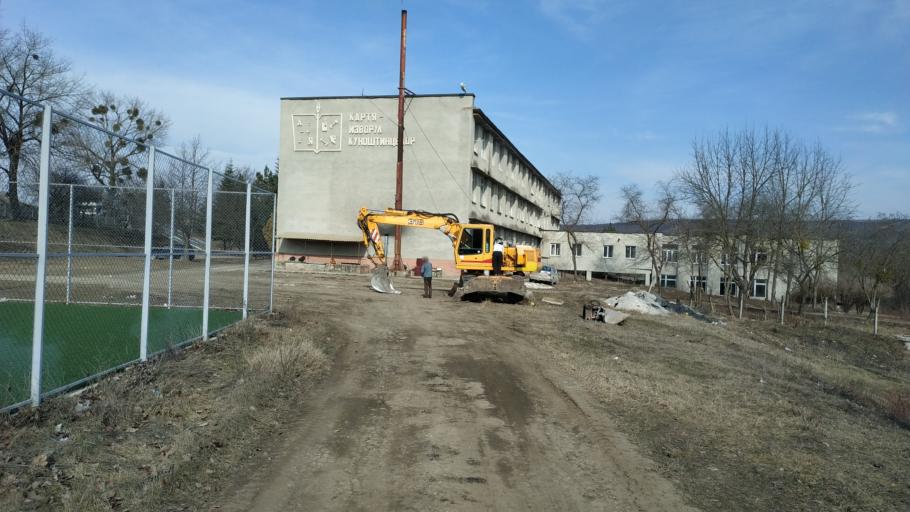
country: MD
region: Nisporeni
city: Nisporeni
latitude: 47.1936
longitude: 28.0670
